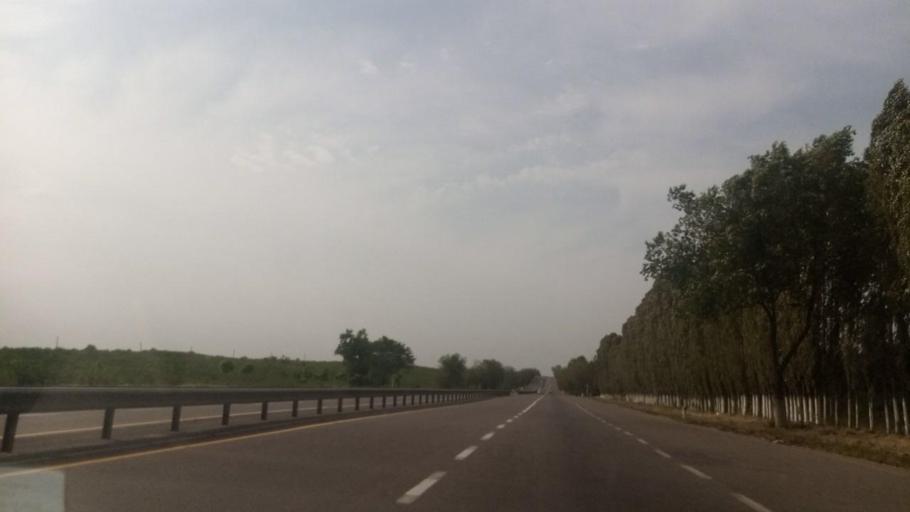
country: UZ
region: Toshkent
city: Tuytepa
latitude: 41.0903
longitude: 69.4633
